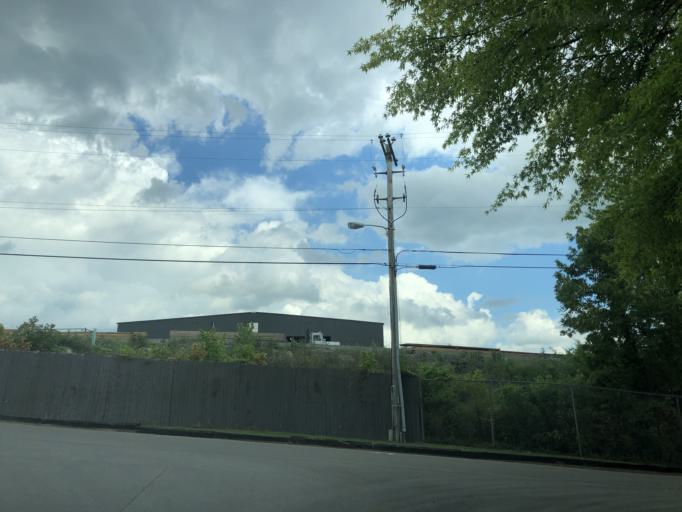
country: US
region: Tennessee
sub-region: Davidson County
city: Nashville
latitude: 36.2232
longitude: -86.7631
